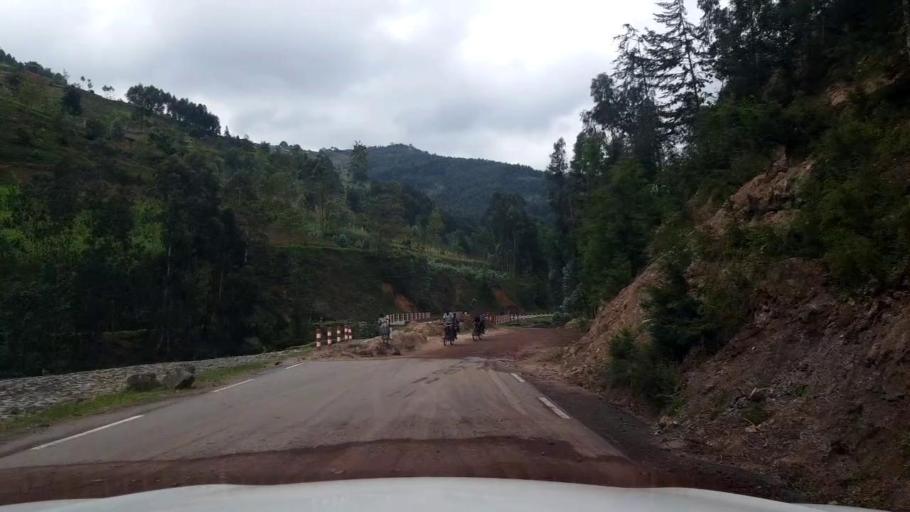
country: RW
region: Northern Province
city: Musanze
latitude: -1.6971
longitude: 29.5576
